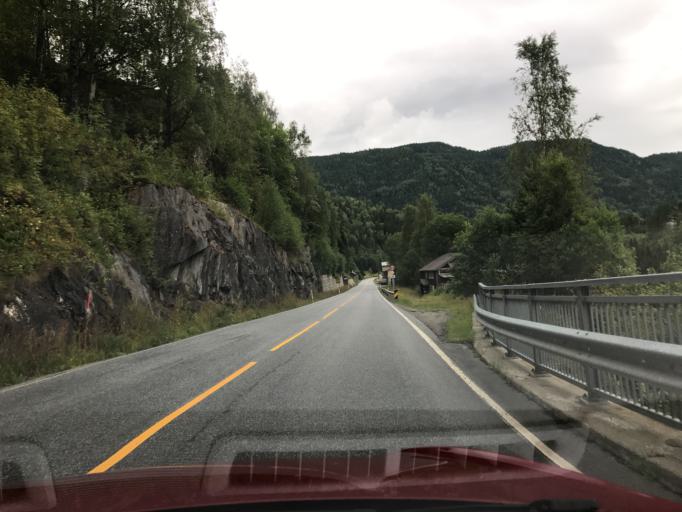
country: NO
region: Buskerud
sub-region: Nore og Uvdal
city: Rodberg
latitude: 60.2624
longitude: 8.9830
